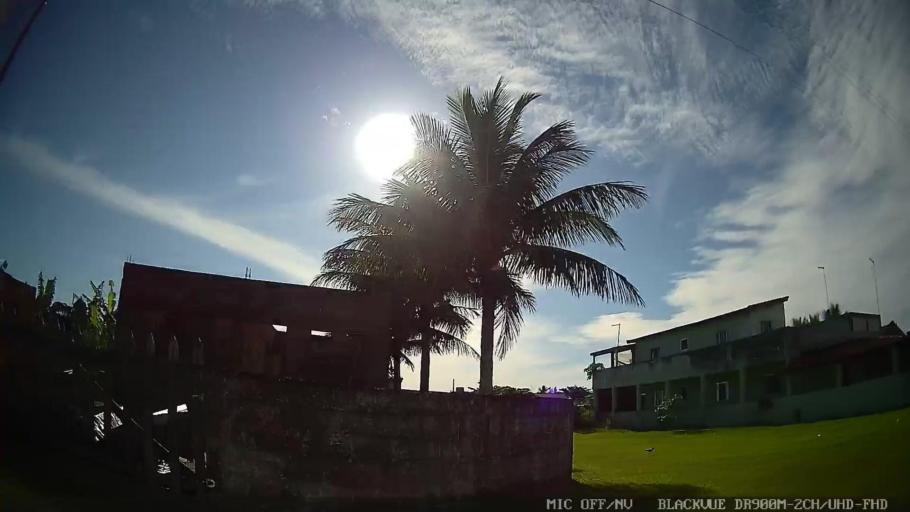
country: BR
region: Sao Paulo
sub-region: Iguape
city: Iguape
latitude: -24.7632
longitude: -47.5776
